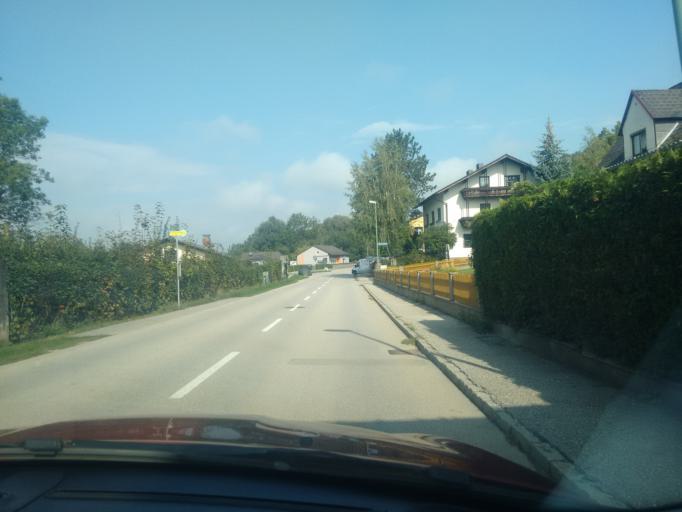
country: AT
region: Upper Austria
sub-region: Wels-Land
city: Steinhaus
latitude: 48.1326
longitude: 14.0094
